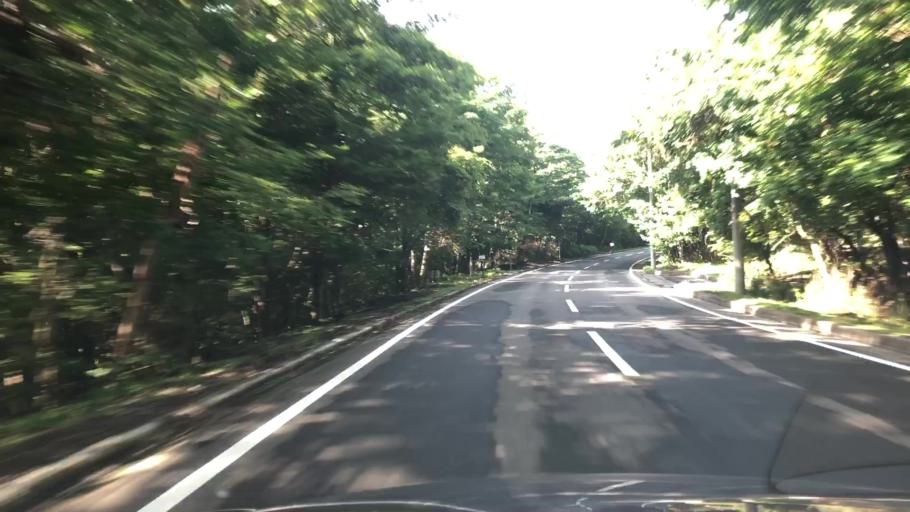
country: JP
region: Shizuoka
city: Gotemba
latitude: 35.3154
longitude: 138.7870
